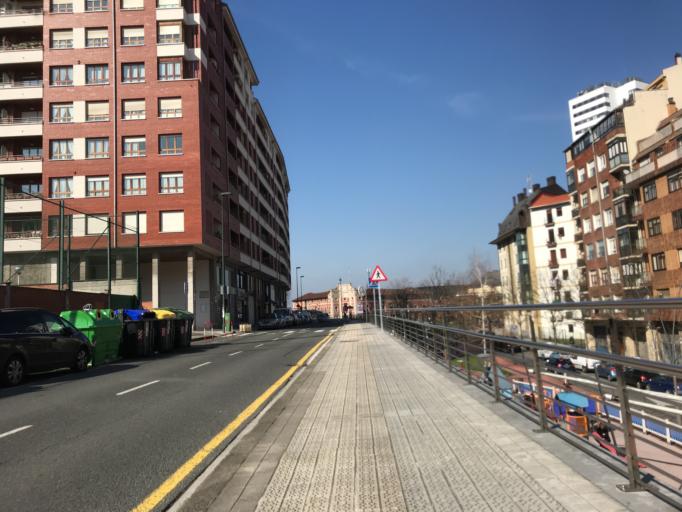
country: ES
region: Basque Country
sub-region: Bizkaia
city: Bilbao
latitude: 43.2577
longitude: -2.9515
